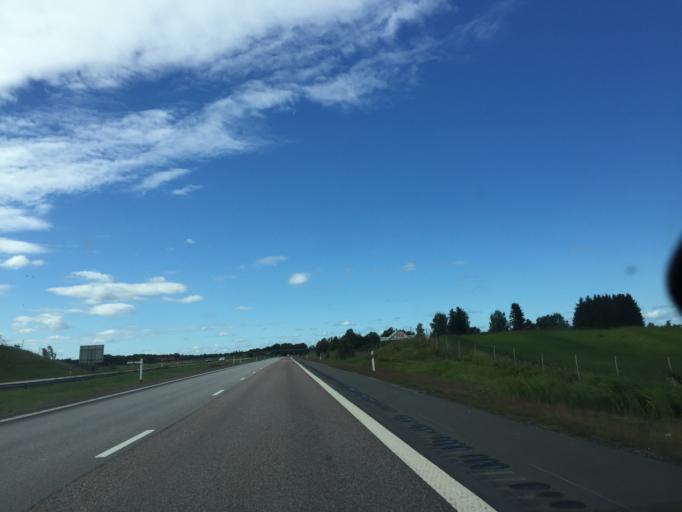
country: SE
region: OErebro
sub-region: Lindesbergs Kommun
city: Frovi
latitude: 59.3072
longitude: 15.3814
